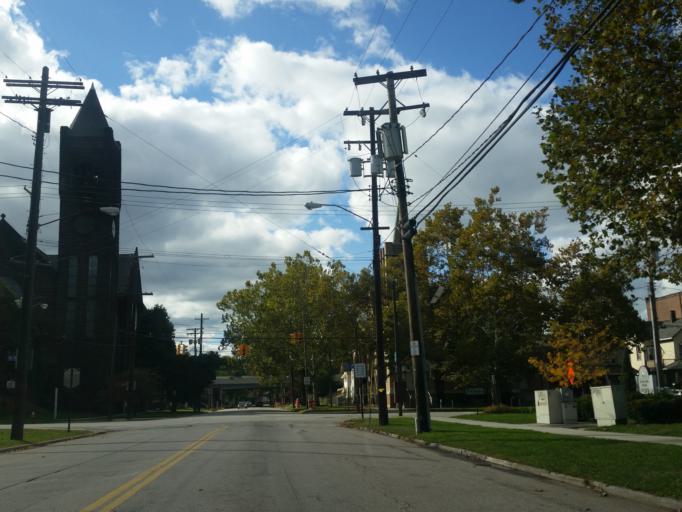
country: US
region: Ohio
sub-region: Cuyahoga County
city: Cleveland
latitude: 41.4775
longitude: -81.6906
